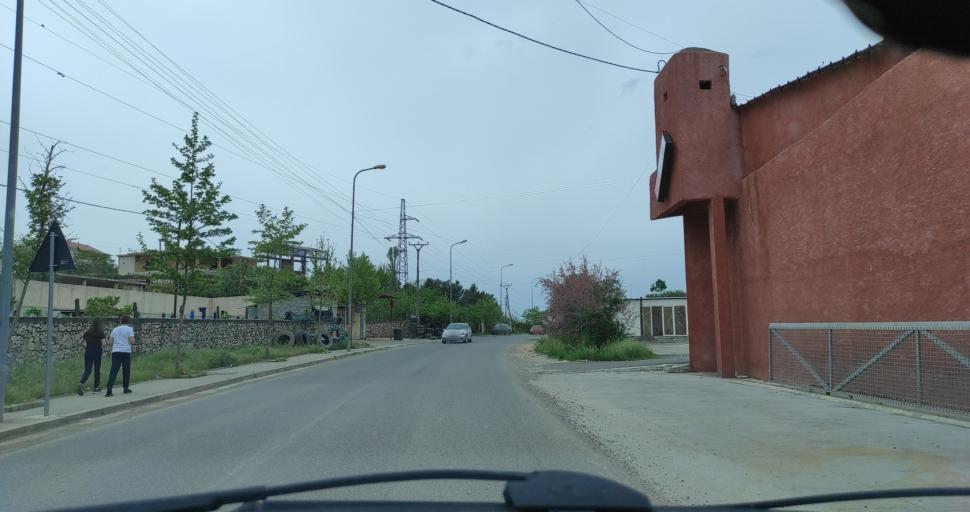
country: AL
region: Lezhe
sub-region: Rrethi i Kurbinit
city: Lac
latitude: 41.6221
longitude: 19.7089
